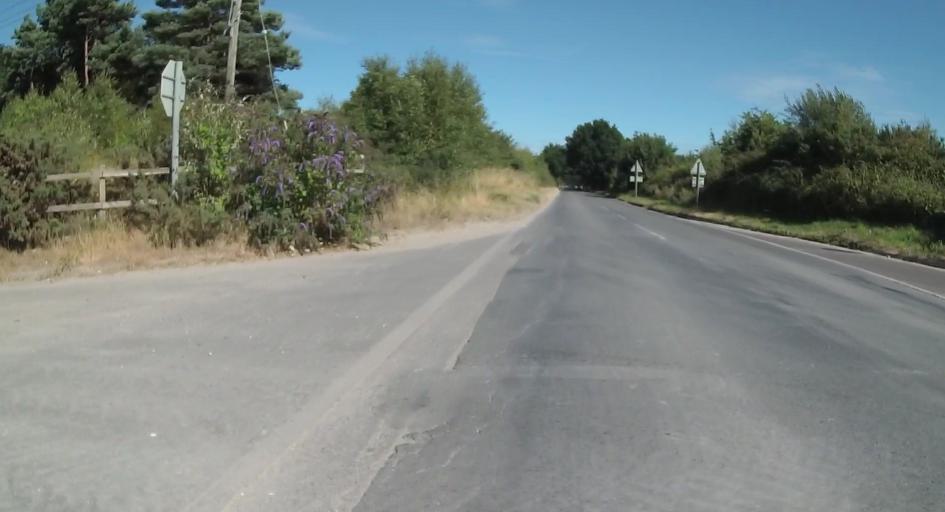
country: GB
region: England
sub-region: Dorset
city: Wool
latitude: 50.6907
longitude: -2.1653
